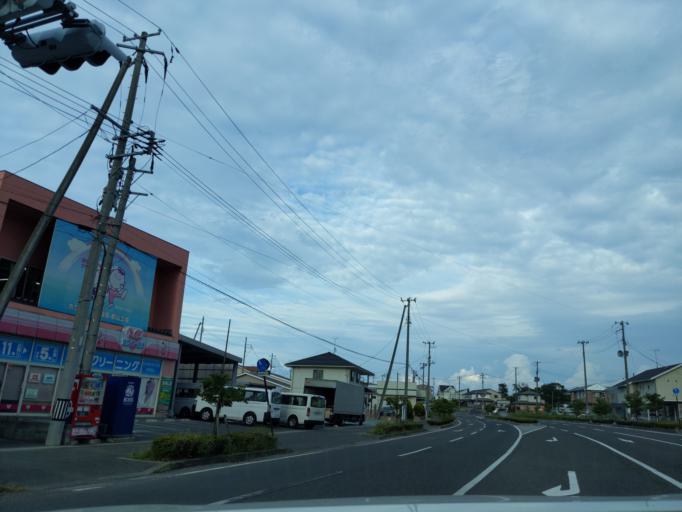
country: JP
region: Fukushima
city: Koriyama
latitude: 37.4247
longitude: 140.3372
